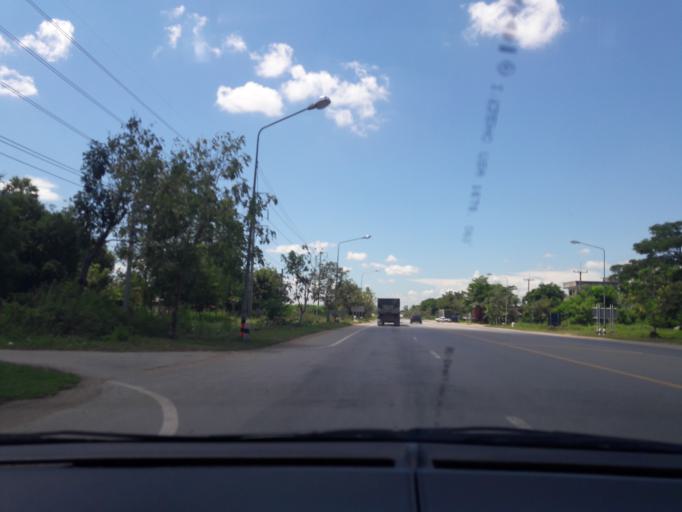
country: TH
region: Kanchanaburi
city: Phanom Thuan
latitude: 14.0456
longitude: 99.7836
